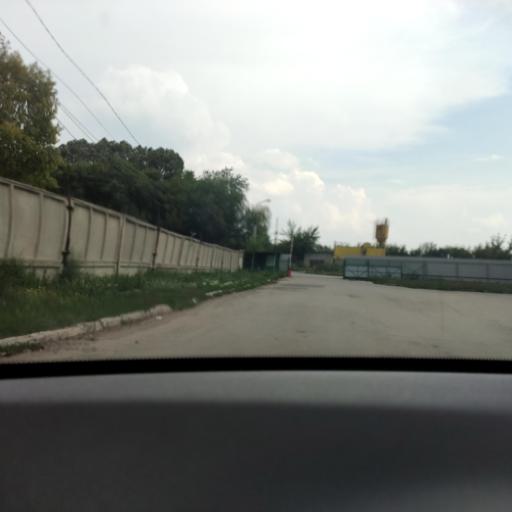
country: RU
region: Samara
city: Samara
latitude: 53.1932
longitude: 50.2709
